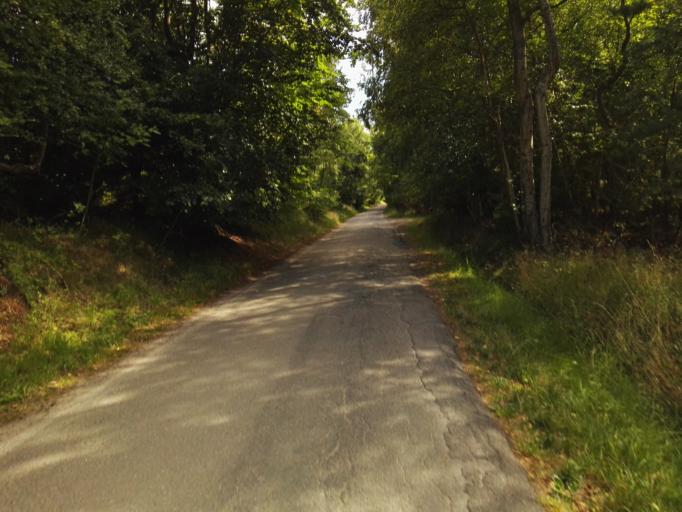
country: DK
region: Zealand
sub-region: Odsherred Kommune
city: Nykobing Sjaelland
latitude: 55.9413
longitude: 11.7023
